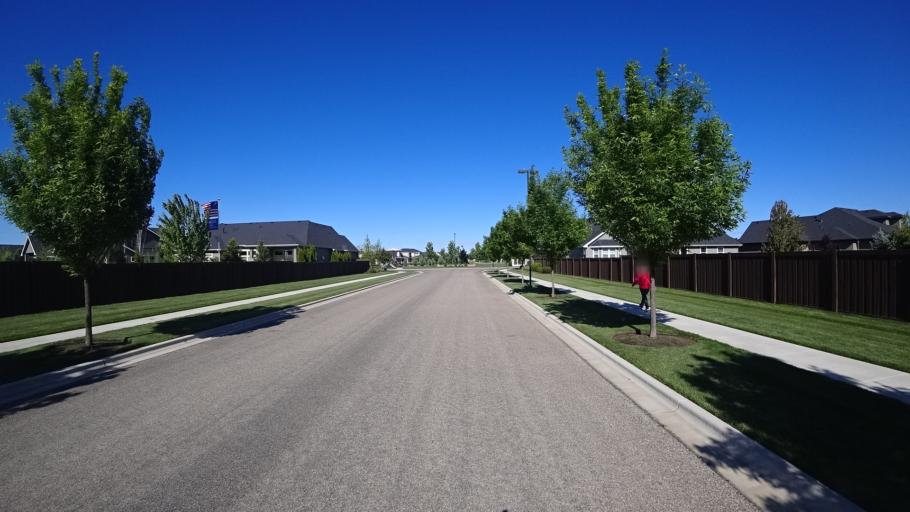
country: US
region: Idaho
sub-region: Ada County
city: Star
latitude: 43.6575
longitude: -116.4445
